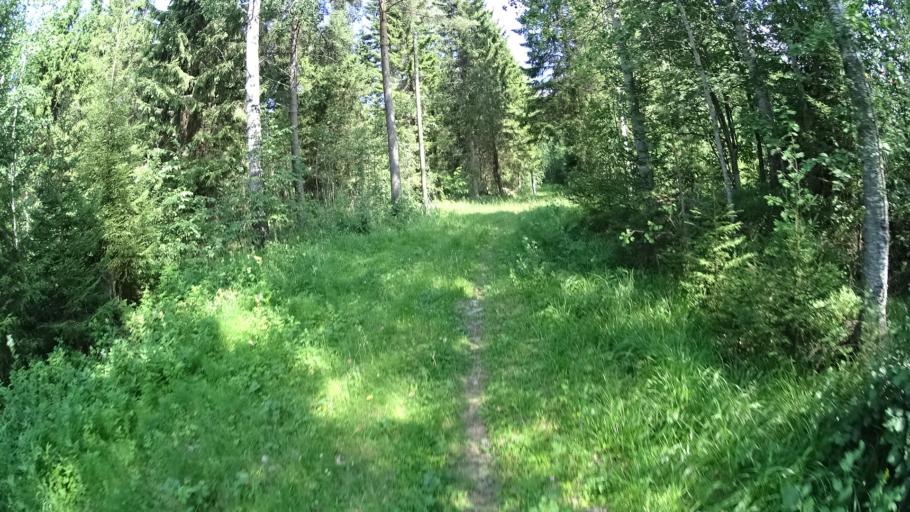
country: FI
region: North Karelia
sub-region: Pielisen Karjala
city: Lieksa
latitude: 63.1202
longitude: 29.8032
